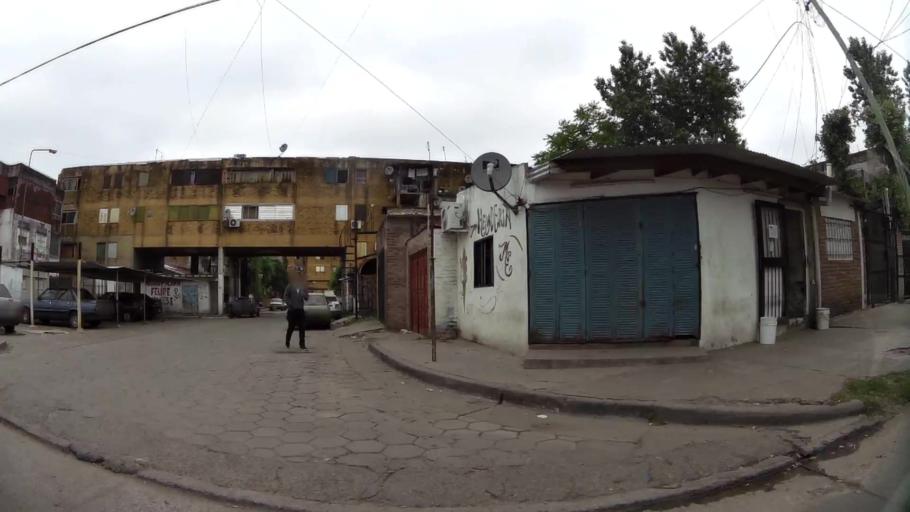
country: AR
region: Buenos Aires
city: San Justo
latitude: -34.7069
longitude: -58.5379
